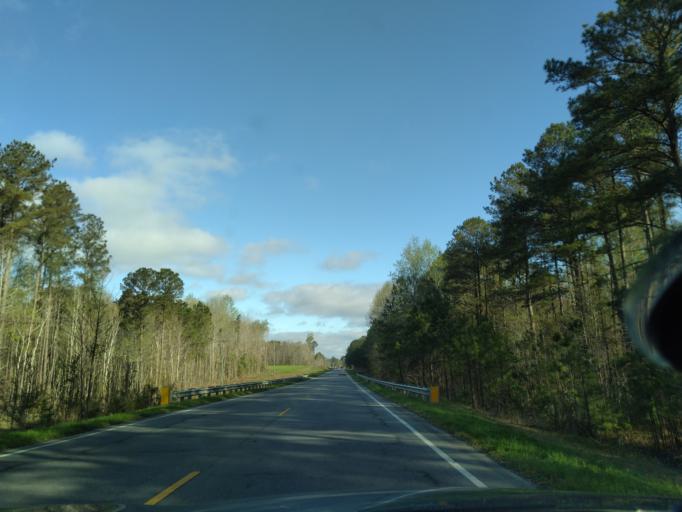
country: US
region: North Carolina
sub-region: Washington County
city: Plymouth
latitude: 36.0232
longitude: -76.7807
